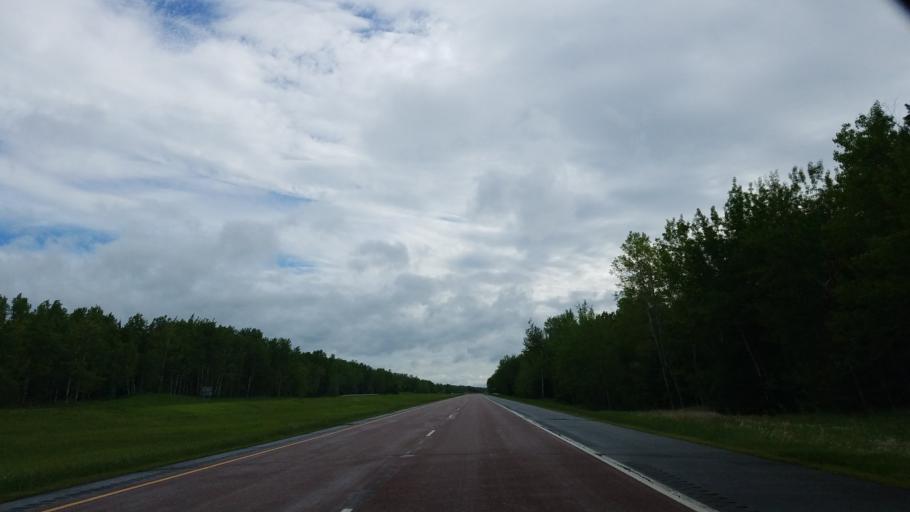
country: US
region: Minnesota
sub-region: Saint Louis County
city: Arnold
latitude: 46.8743
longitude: -91.9483
